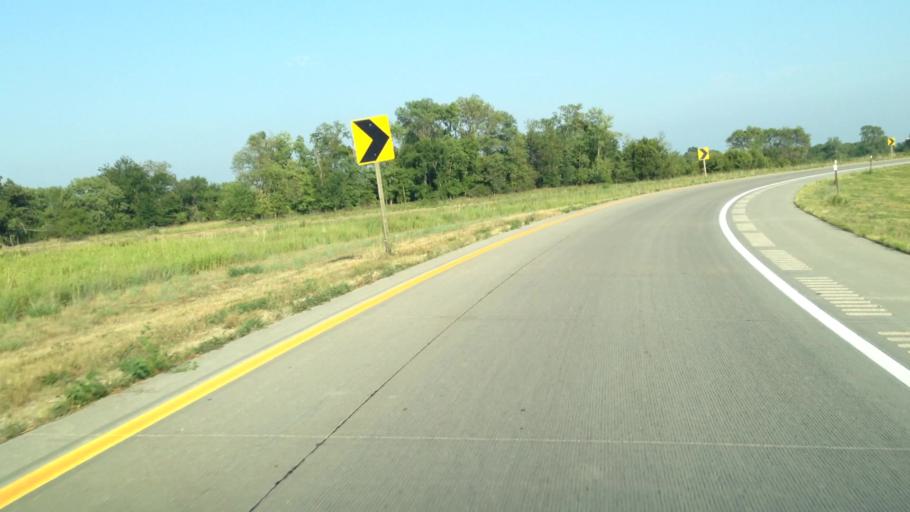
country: US
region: Kansas
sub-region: Franklin County
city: Ottawa
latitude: 38.6387
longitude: -95.2173
